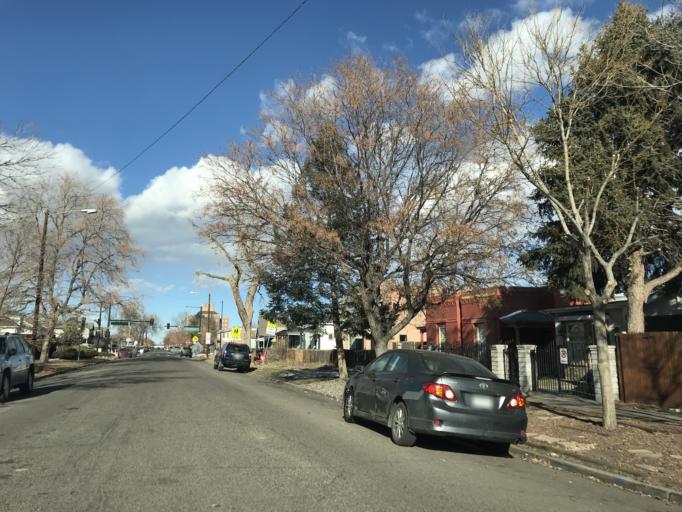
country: US
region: Colorado
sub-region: Denver County
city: Denver
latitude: 39.7609
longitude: -104.9722
